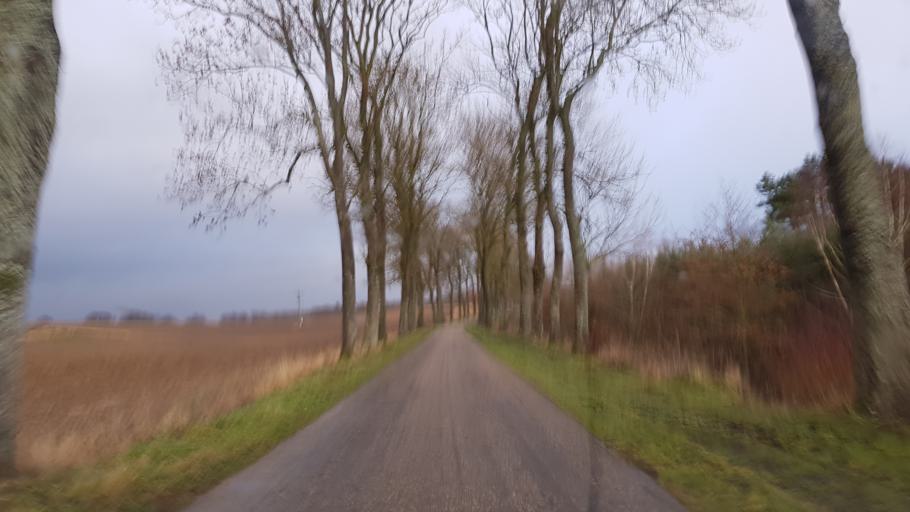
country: PL
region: West Pomeranian Voivodeship
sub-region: Powiat swidwinski
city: Rabino
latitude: 53.9409
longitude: 15.9466
